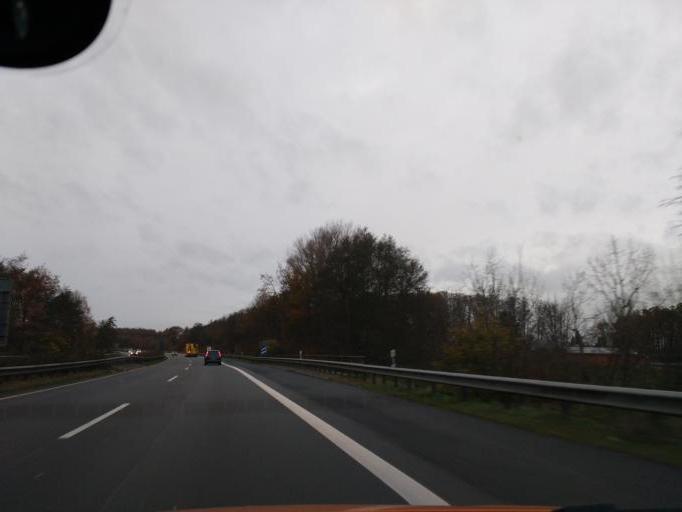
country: DE
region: Lower Saxony
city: Ganderkesee
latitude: 53.0539
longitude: 8.5420
